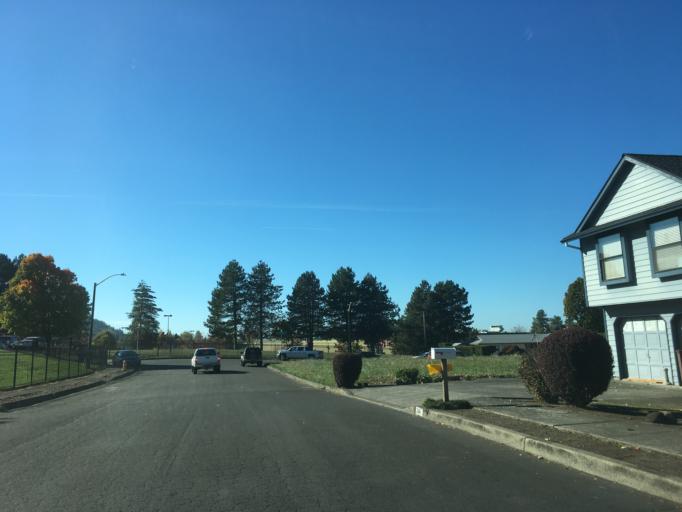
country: US
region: Oregon
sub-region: Multnomah County
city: Gresham
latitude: 45.4948
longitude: -122.4022
